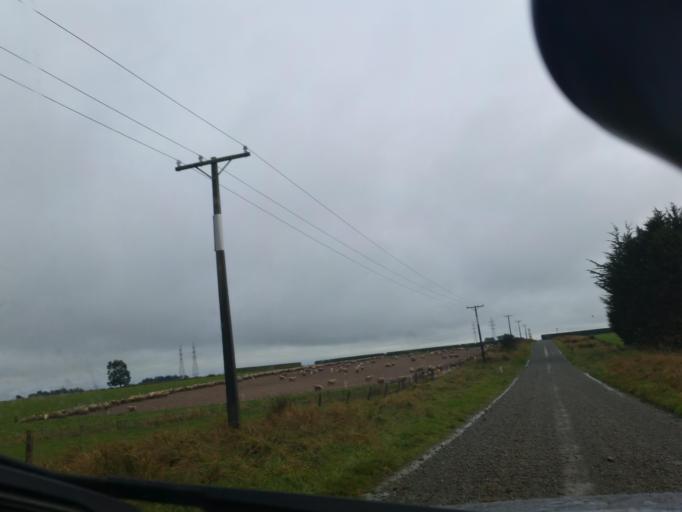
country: NZ
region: Southland
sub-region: Southland District
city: Winton
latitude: -46.2269
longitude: 168.2535
